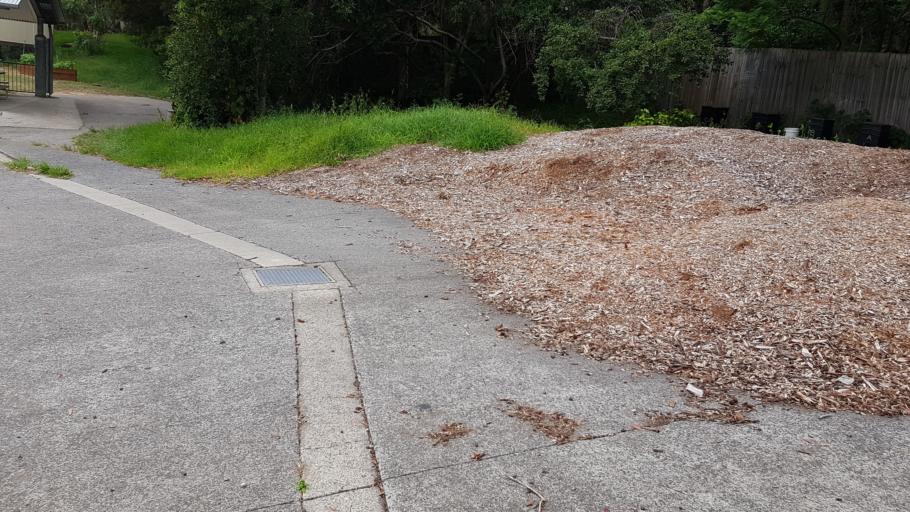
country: AU
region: New South Wales
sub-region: Pittwater
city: North Narrabeen
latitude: -33.7046
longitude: 151.2845
